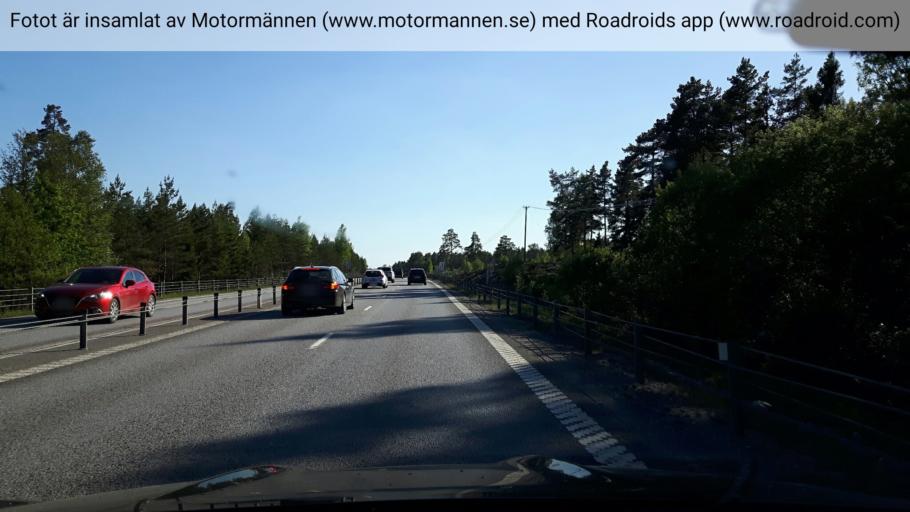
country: SE
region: Stockholm
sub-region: Osterakers Kommun
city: Akersberga
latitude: 59.5845
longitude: 18.2514
